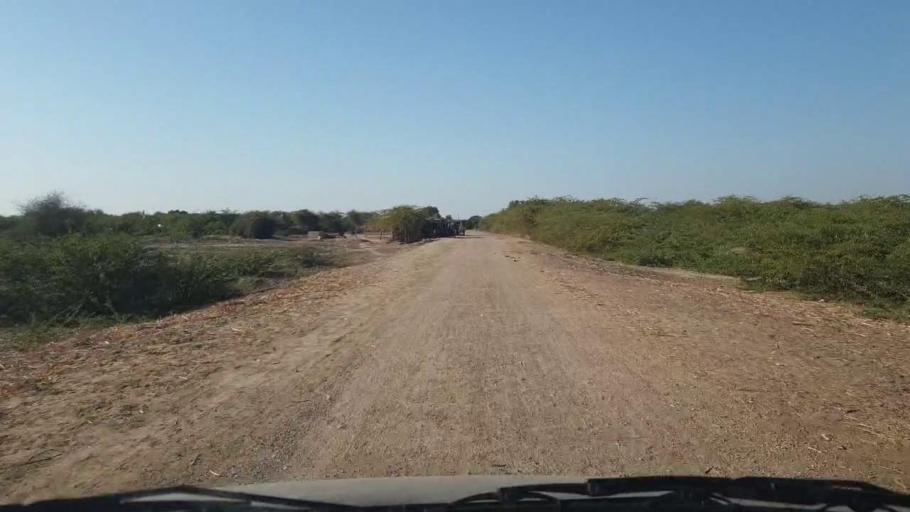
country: PK
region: Sindh
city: Samaro
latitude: 25.3636
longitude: 69.2922
